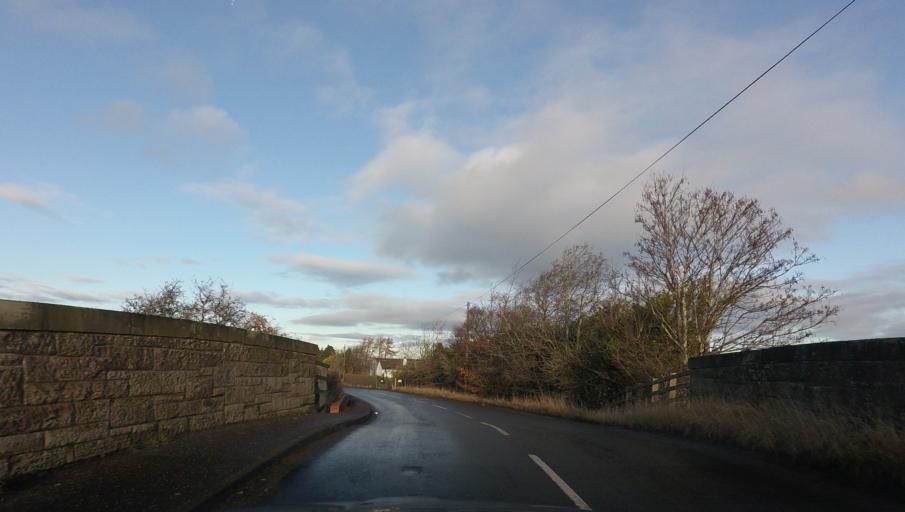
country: GB
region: Scotland
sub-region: West Lothian
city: East Calder
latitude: 55.8960
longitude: -3.4430
